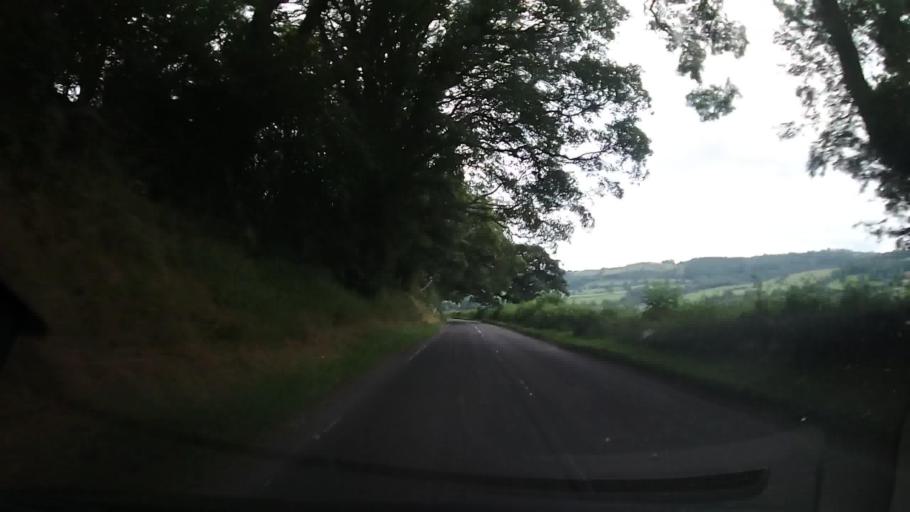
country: GB
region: Wales
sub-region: Sir Powys
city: Llanfechain
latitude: 52.8117
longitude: -3.2343
